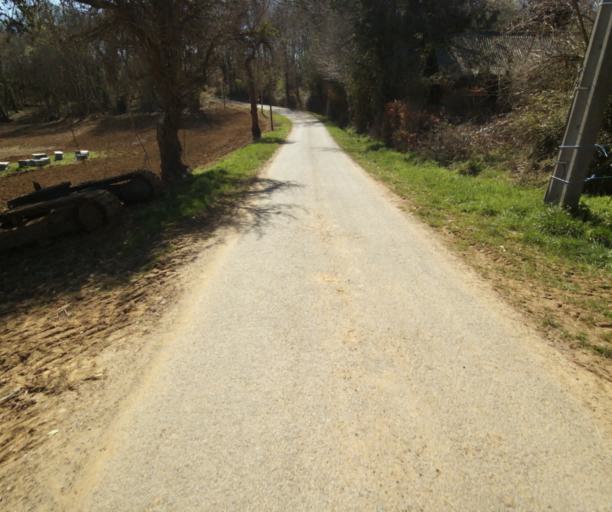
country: FR
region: Limousin
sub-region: Departement de la Correze
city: Uzerche
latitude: 45.3923
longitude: 1.6074
